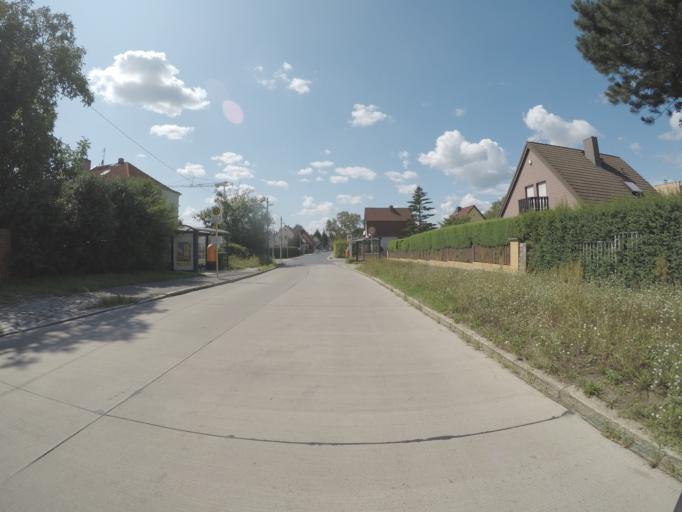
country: DE
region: Berlin
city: Mahlsdorf
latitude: 52.5096
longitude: 13.6064
